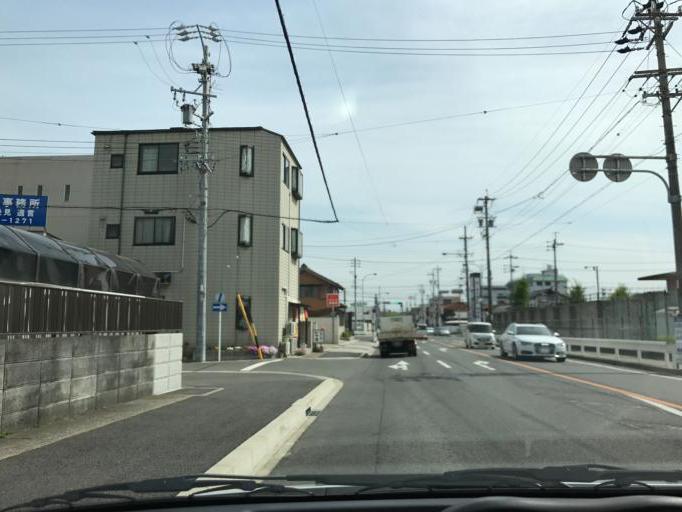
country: JP
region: Aichi
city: Nagoya-shi
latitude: 35.1215
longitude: 136.9614
